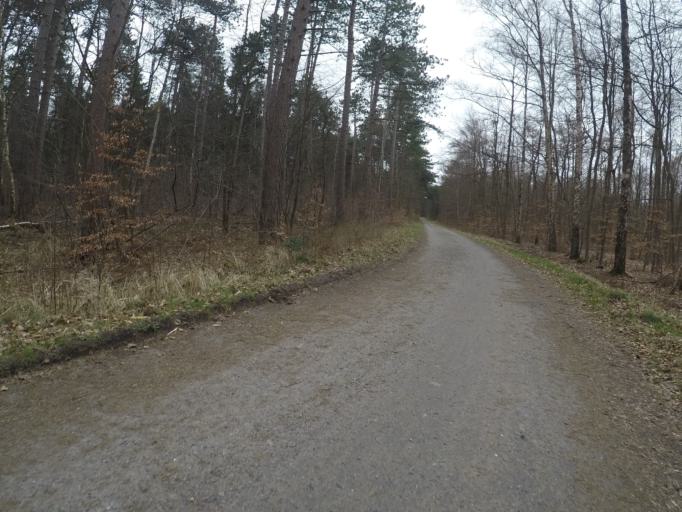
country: DE
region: Lower Saxony
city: Nordholz
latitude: 53.8190
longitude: 8.6378
